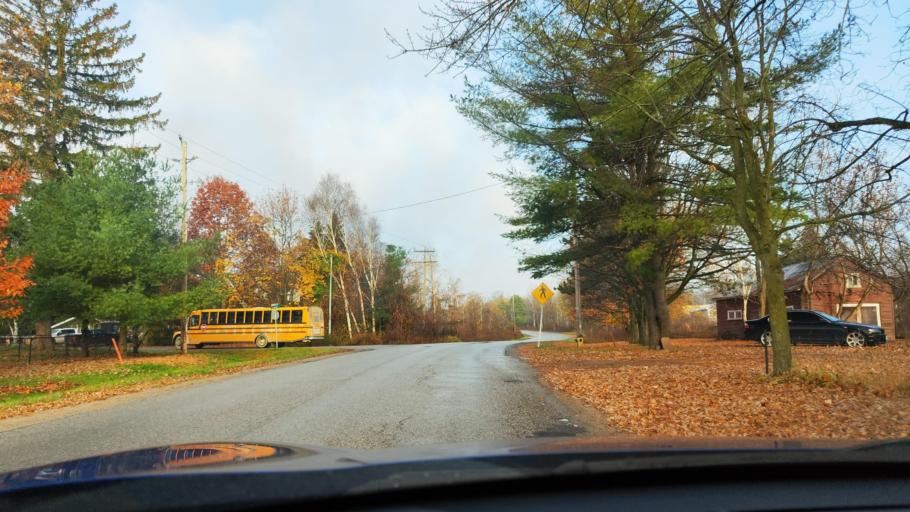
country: CA
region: Ontario
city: Angus
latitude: 44.3596
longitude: -79.9749
